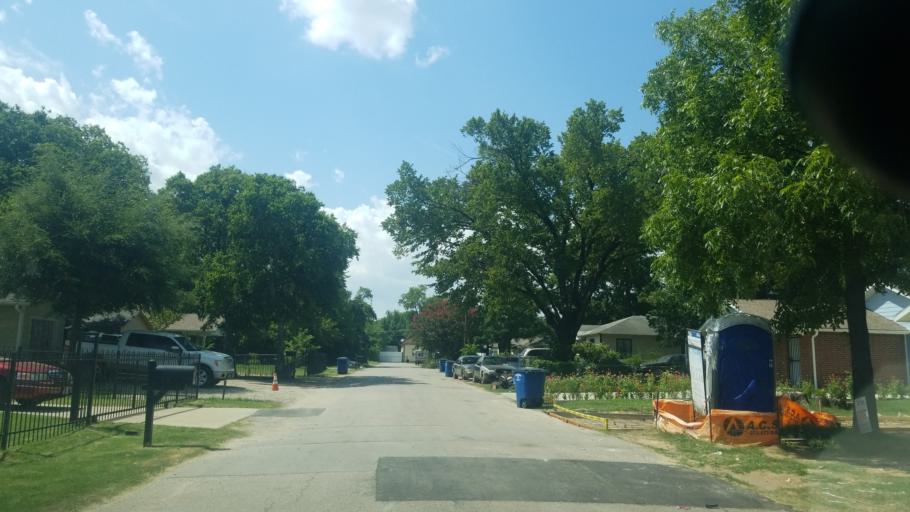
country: US
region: Texas
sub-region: Dallas County
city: Hutchins
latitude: 32.7136
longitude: -96.7480
